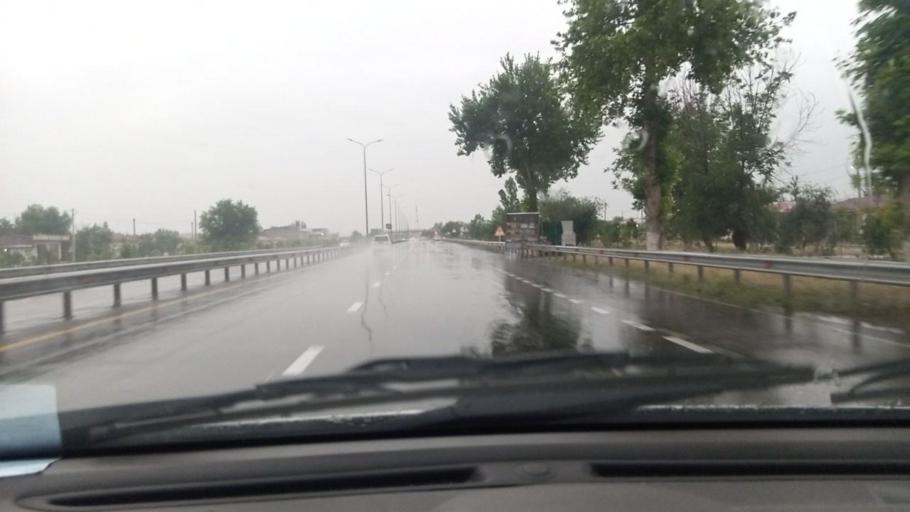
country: UZ
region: Toshkent
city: Tuytepa
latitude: 41.1344
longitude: 69.4350
